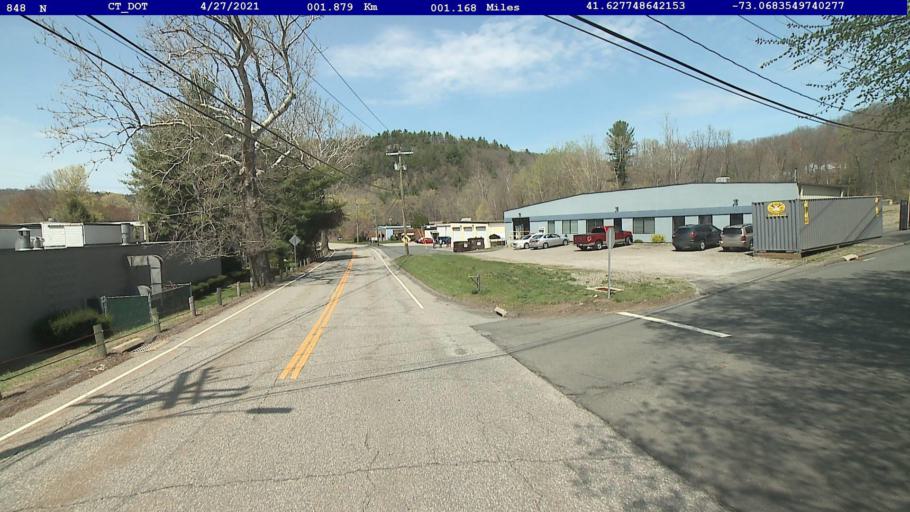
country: US
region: Connecticut
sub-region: Litchfield County
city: Oakville
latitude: 41.6277
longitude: -73.0680
